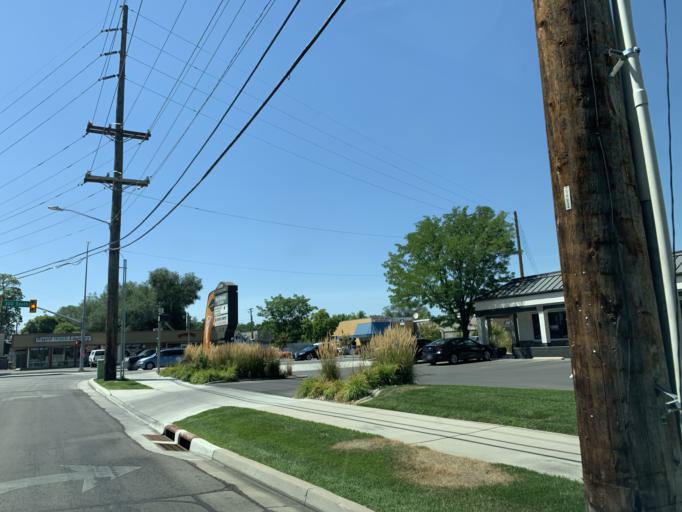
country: US
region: Utah
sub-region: Utah County
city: Provo
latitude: 40.2301
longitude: -111.6466
